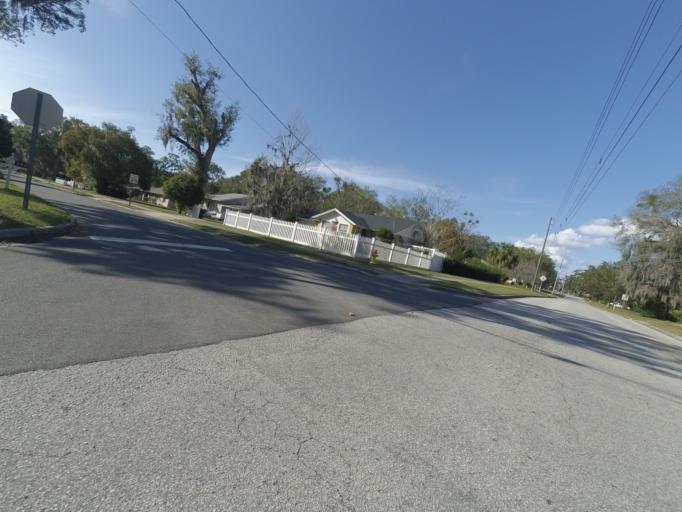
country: US
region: Florida
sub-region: Lake County
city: Mount Dora
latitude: 28.8042
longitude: -81.6364
